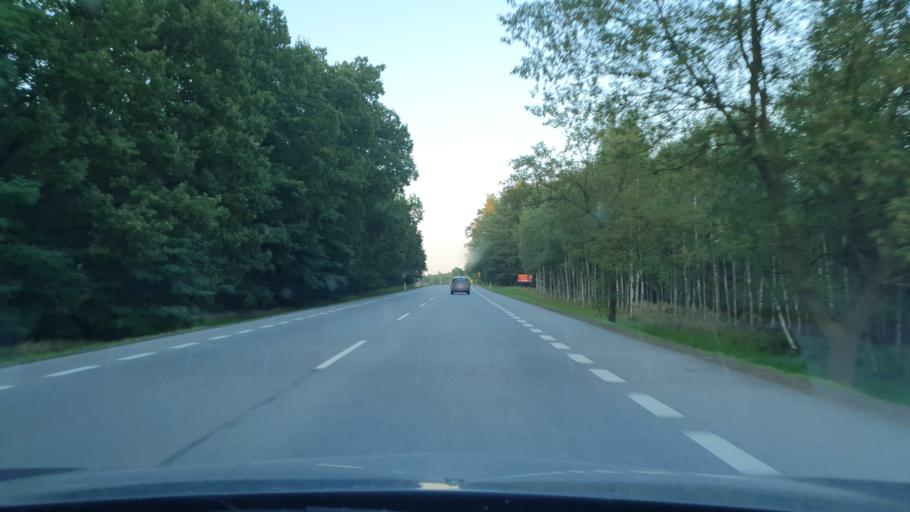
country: PL
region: Pomeranian Voivodeship
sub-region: Powiat leborski
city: Nowa Wies Leborska
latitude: 54.4973
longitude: 17.6195
